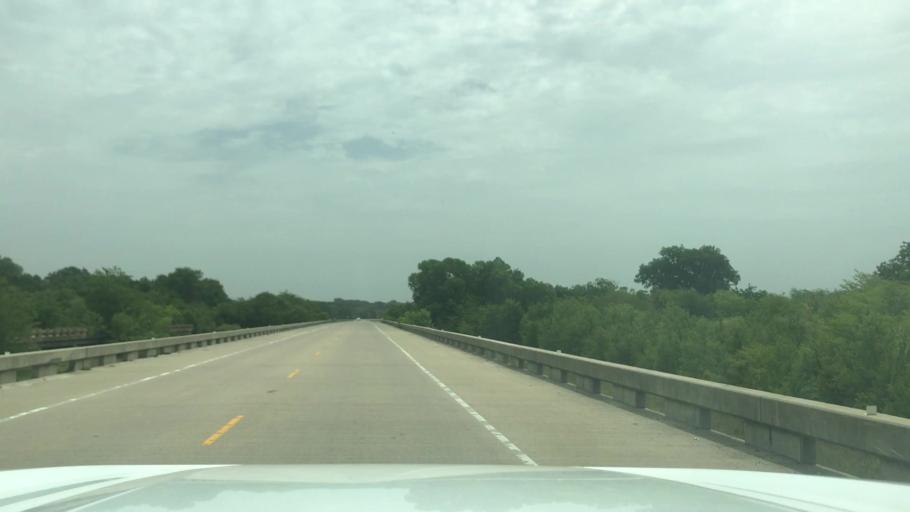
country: US
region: Texas
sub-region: Hamilton County
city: Hico
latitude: 32.0393
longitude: -98.1099
